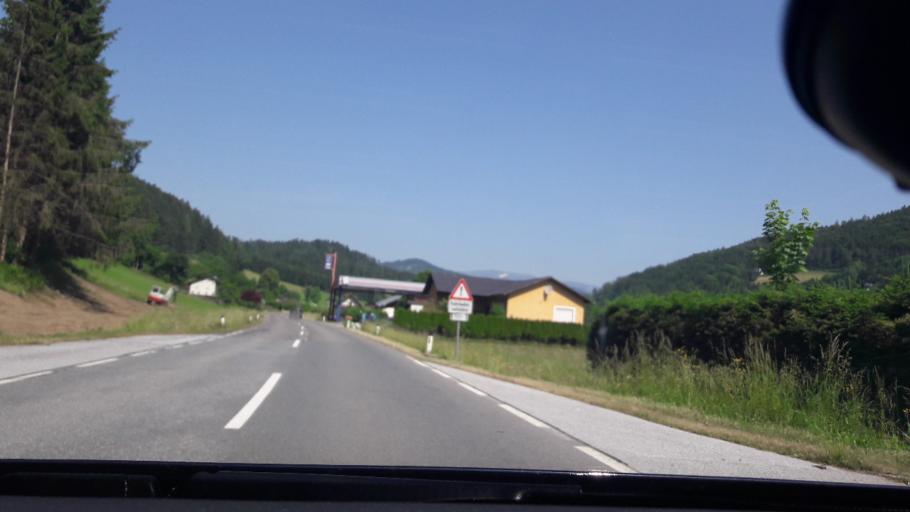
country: AT
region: Styria
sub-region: Politischer Bezirk Voitsberg
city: Sodingberg
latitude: 47.0934
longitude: 15.1831
